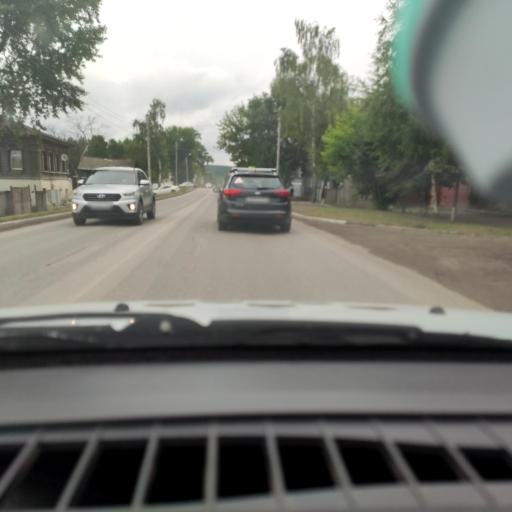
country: RU
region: Perm
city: Kungur
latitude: 57.4350
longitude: 56.9491
